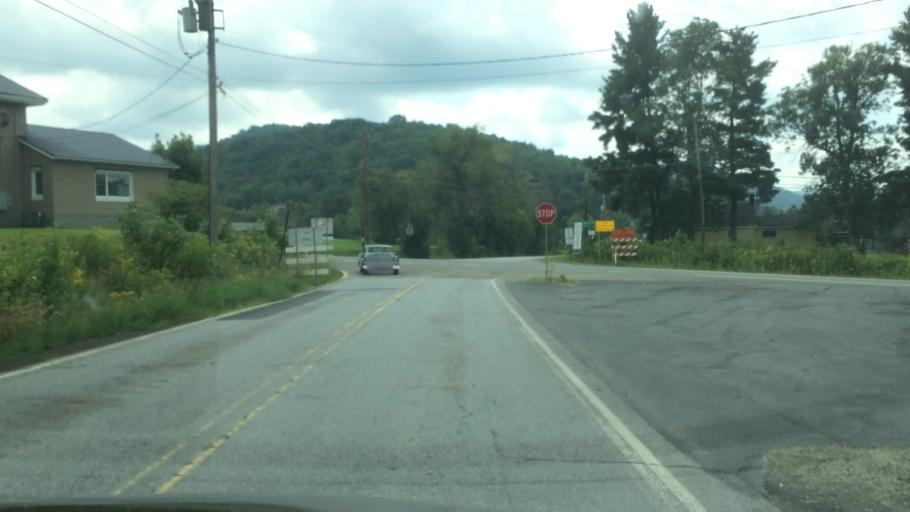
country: US
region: Pennsylvania
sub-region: McKean County
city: Bradford
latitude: 41.9135
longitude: -78.6422
